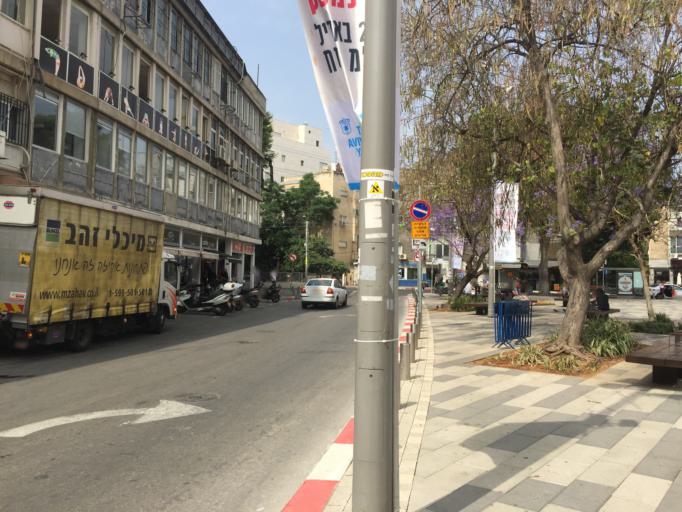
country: IL
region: Tel Aviv
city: Tel Aviv
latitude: 32.0705
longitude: 34.7832
